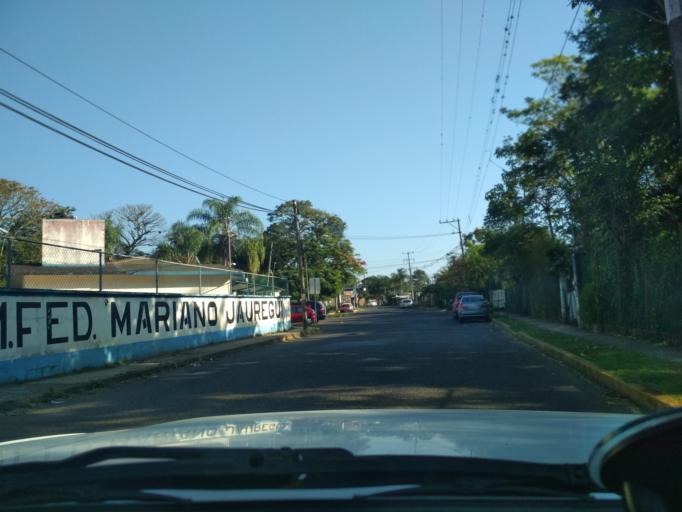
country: MX
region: Veracruz
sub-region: Fortin
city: Fraccionamiento Villas de la Llave
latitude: 18.9178
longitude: -96.9896
